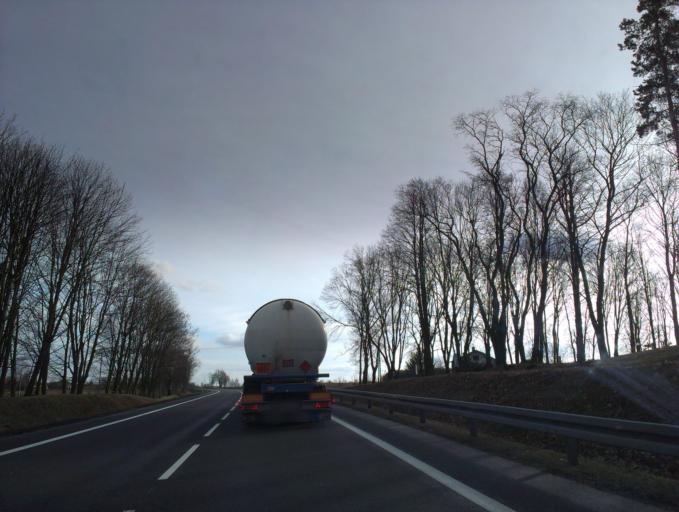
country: PL
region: Kujawsko-Pomorskie
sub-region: Powiat lipnowski
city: Kikol
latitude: 52.8926
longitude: 19.1247
